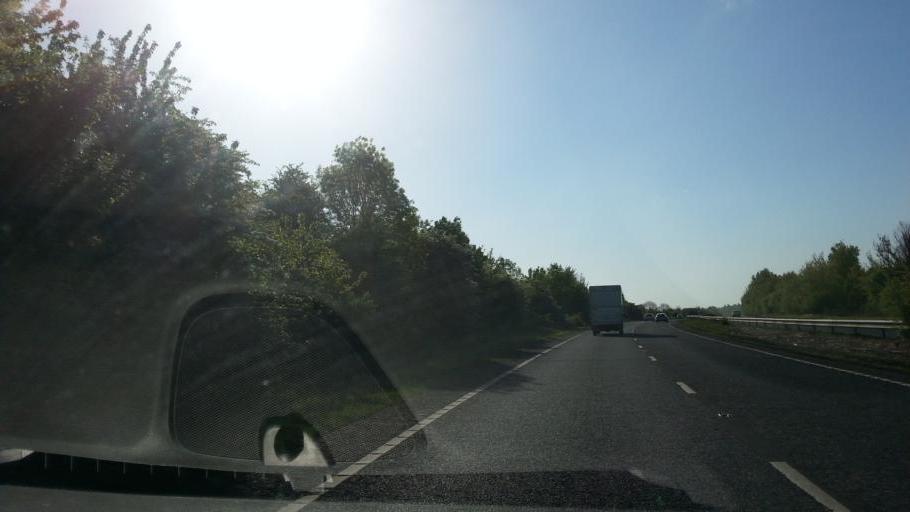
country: GB
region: England
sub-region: Peterborough
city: Castor
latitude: 52.5809
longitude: -0.3454
